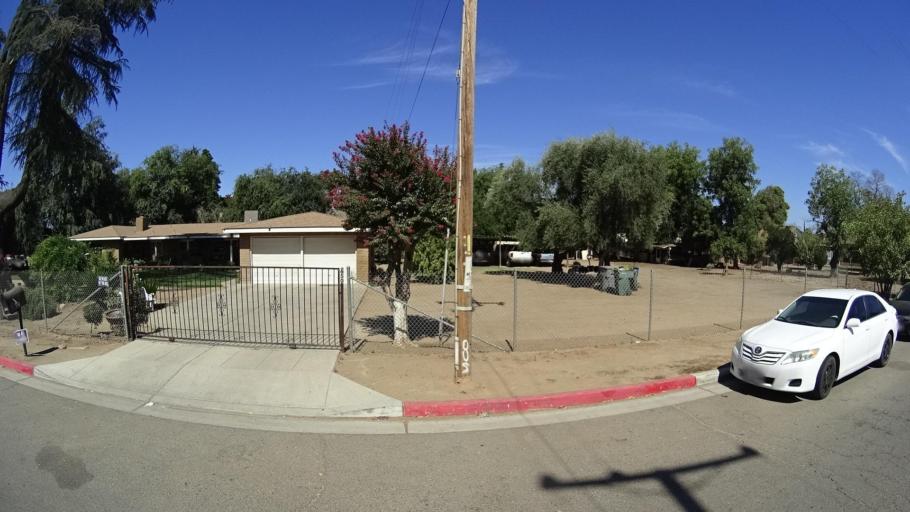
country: US
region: California
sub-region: Fresno County
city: Sunnyside
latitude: 36.7365
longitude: -119.7115
